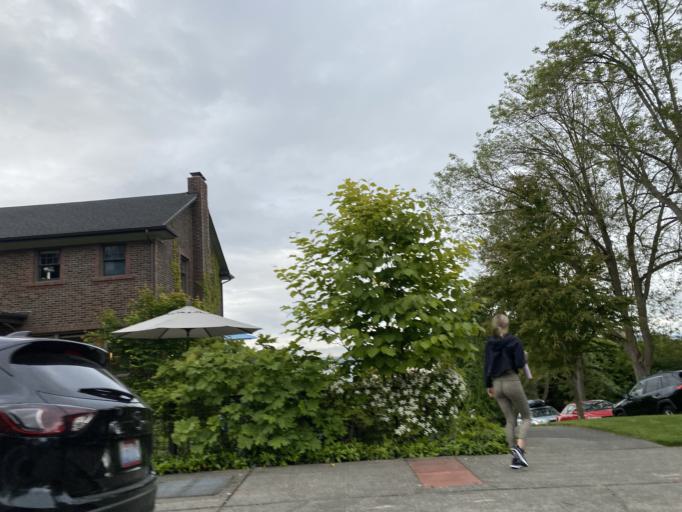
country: US
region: Washington
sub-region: King County
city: Seattle
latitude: 47.6288
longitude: -122.3591
